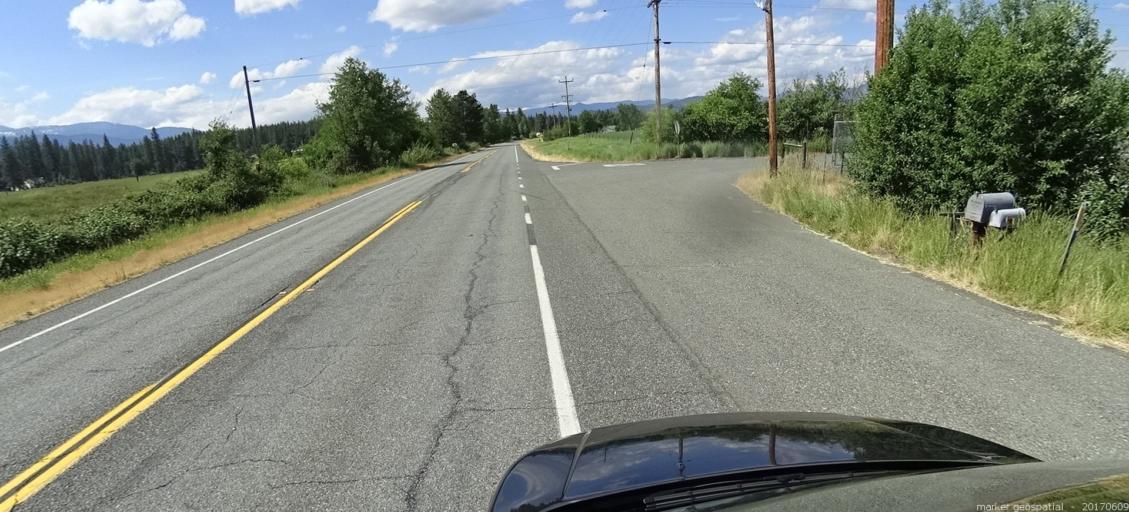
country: US
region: California
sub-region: Siskiyou County
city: Yreka
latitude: 41.4931
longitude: -122.9061
